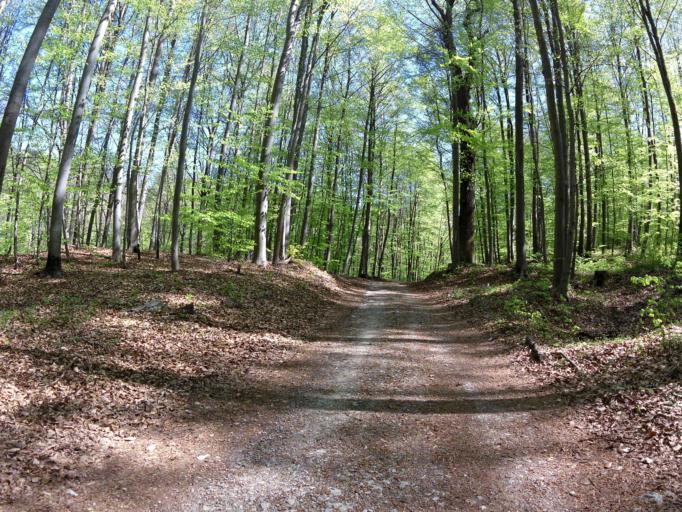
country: DE
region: Thuringia
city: Krauthausen
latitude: 50.9850
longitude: 10.2204
